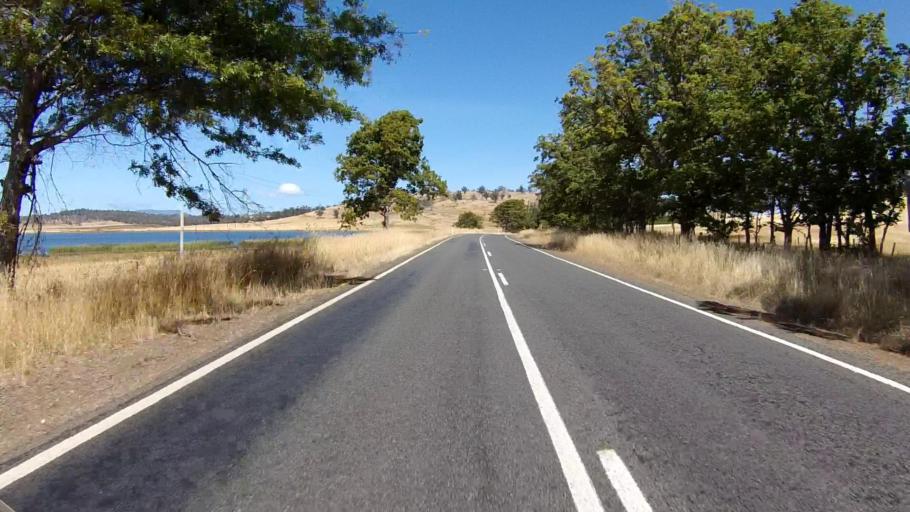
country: AU
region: Tasmania
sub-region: Sorell
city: Sorell
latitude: -42.4863
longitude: 147.9345
